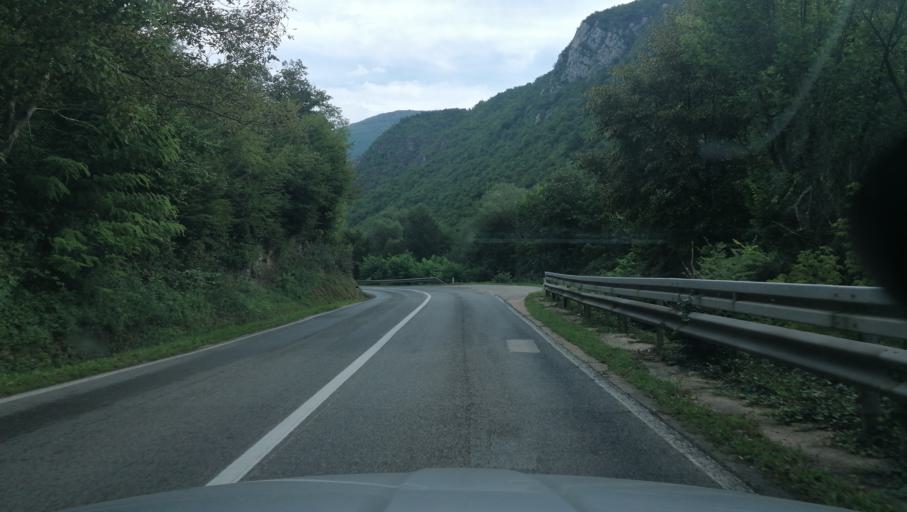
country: BA
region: Republika Srpska
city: Hiseti
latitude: 44.6278
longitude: 17.1522
